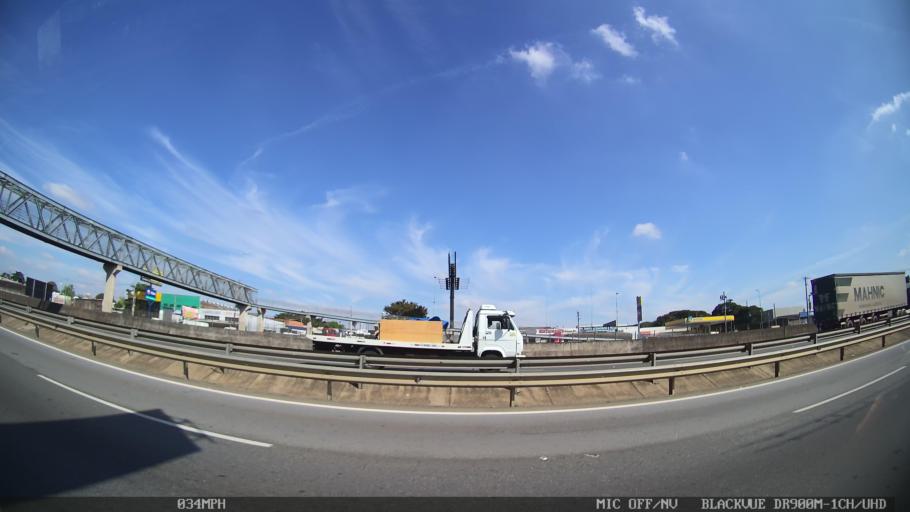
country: BR
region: Sao Paulo
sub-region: Hortolandia
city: Hortolandia
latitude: -22.8491
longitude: -47.1597
